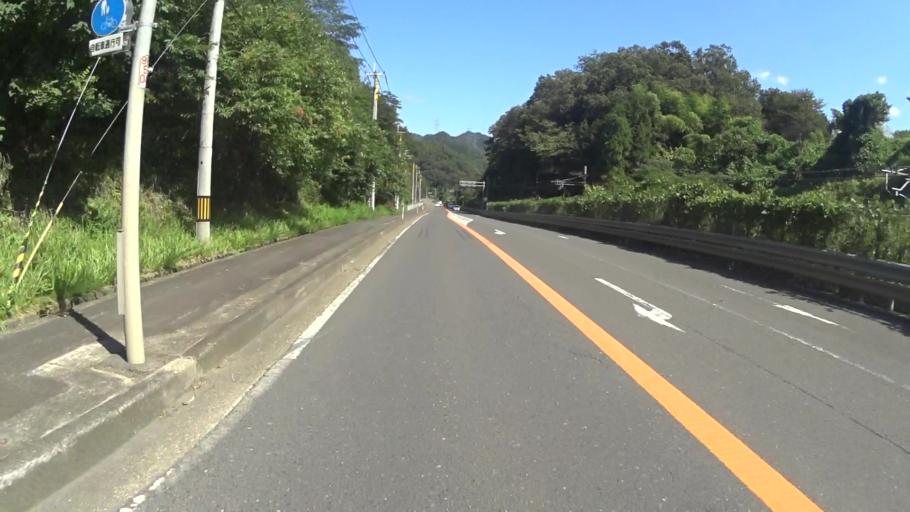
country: JP
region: Kyoto
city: Maizuru
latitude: 35.3630
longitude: 135.3176
